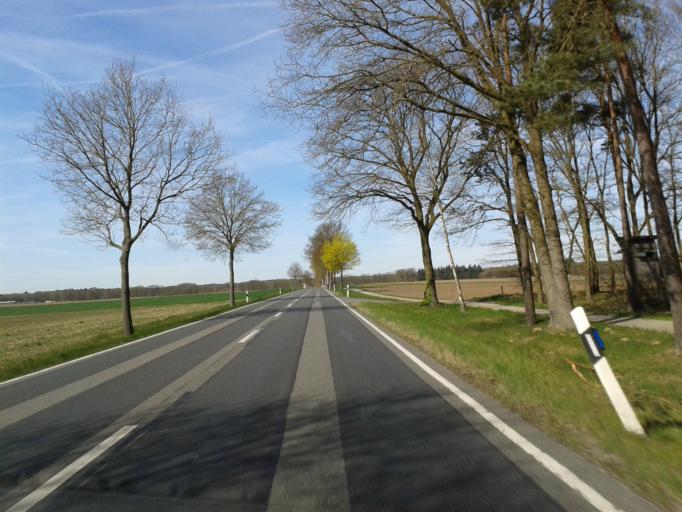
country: DE
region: Lower Saxony
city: Eimke
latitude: 52.9665
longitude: 10.3425
